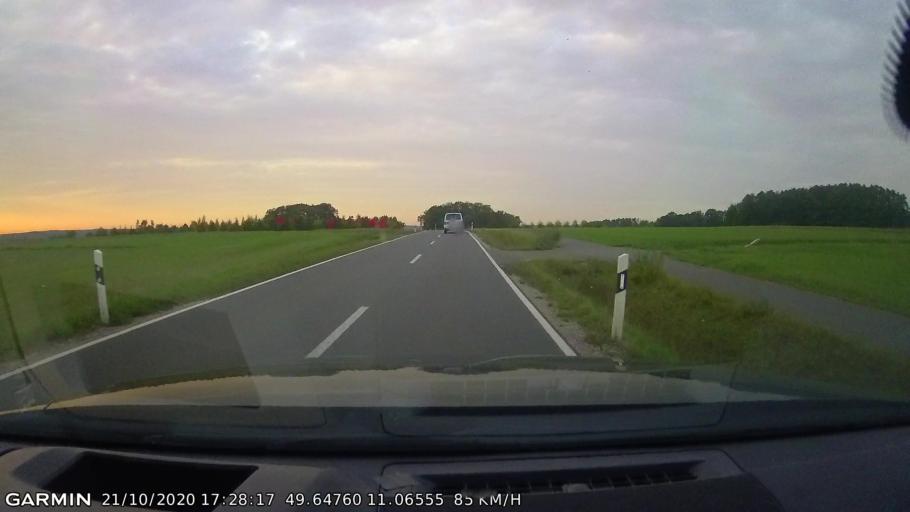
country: DE
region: Bavaria
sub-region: Upper Franconia
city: Langensendelbach
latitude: 49.6477
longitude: 11.0656
